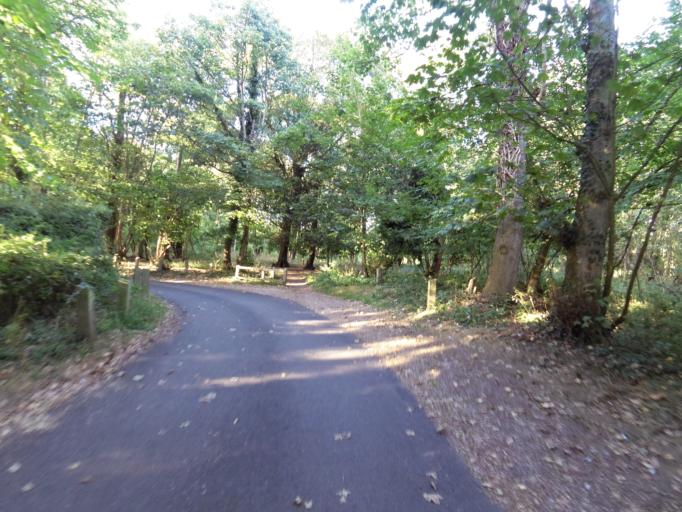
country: GB
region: England
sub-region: Suffolk
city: Kesgrave
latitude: 52.0069
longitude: 1.2333
